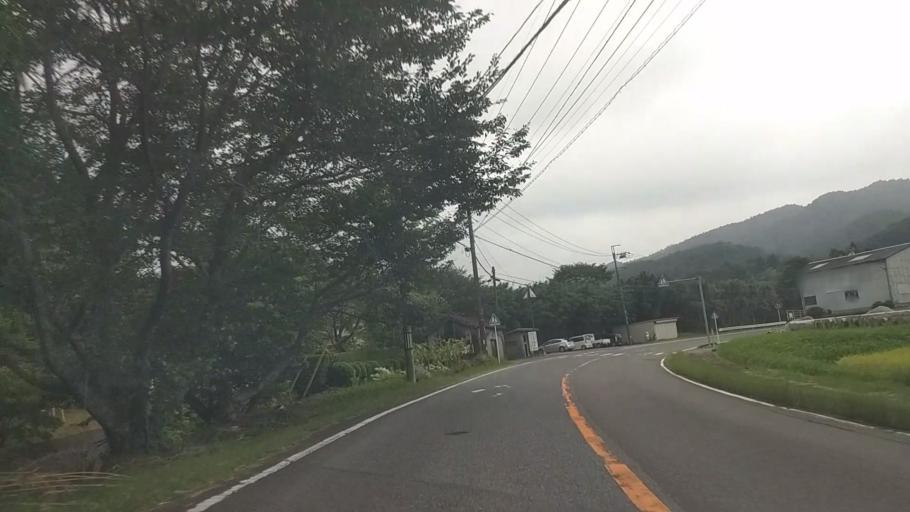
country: JP
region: Chiba
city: Kawaguchi
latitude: 35.1383
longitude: 139.9781
